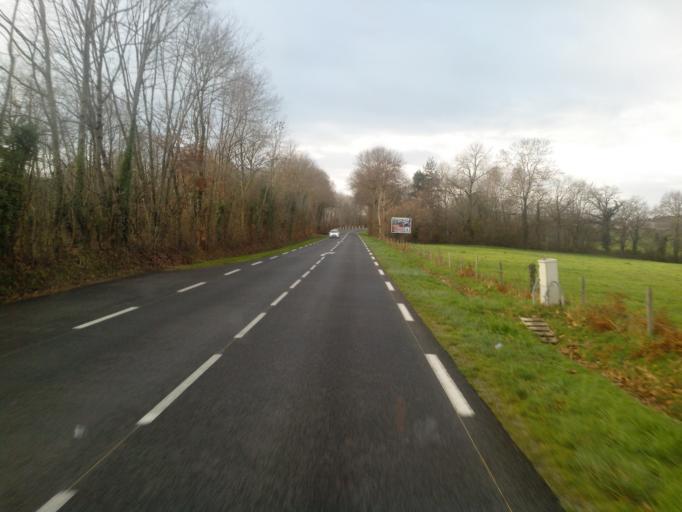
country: FR
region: Limousin
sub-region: Departement de la Haute-Vienne
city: Le Dorat
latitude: 46.2141
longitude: 1.1040
